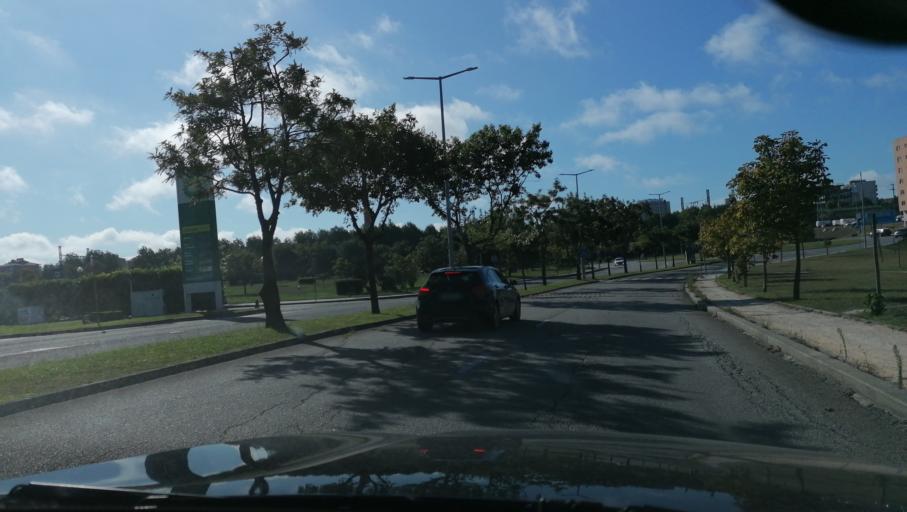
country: PT
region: Aveiro
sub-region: Aveiro
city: Aveiro
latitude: 40.6377
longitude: -8.6397
